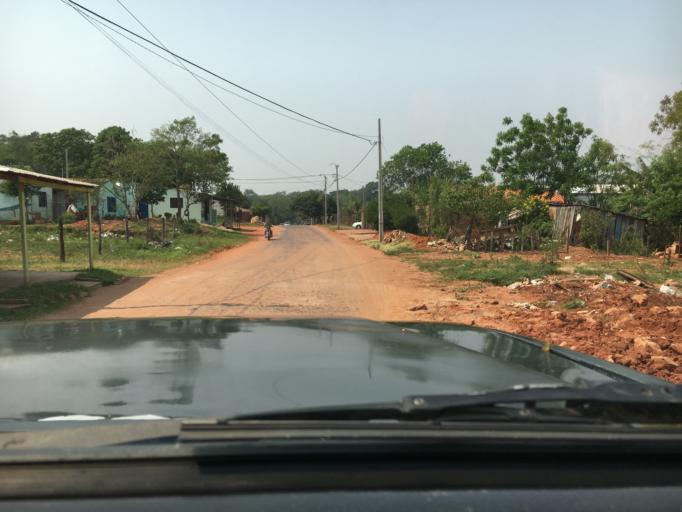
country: PY
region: Central
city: Villa Elisa
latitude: -25.3828
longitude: -57.5729
